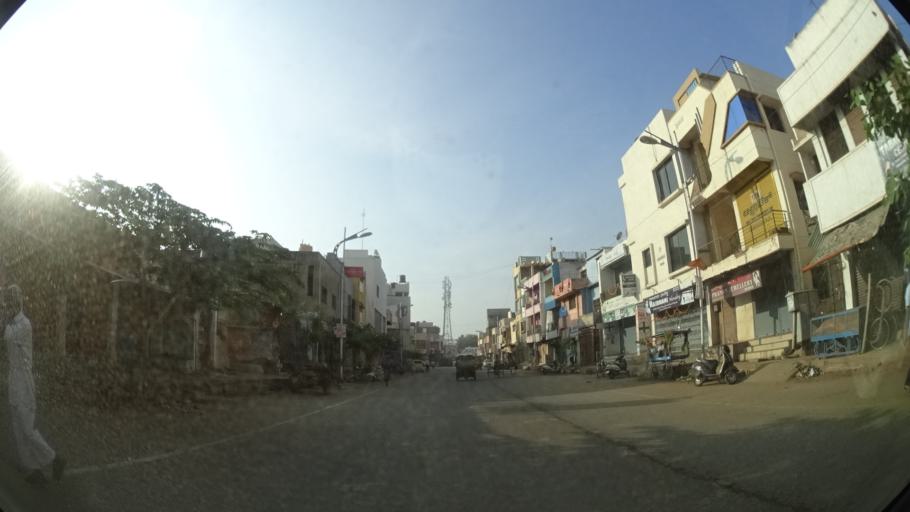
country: IN
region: Karnataka
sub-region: Bellary
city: Hospet
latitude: 15.2688
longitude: 76.3935
